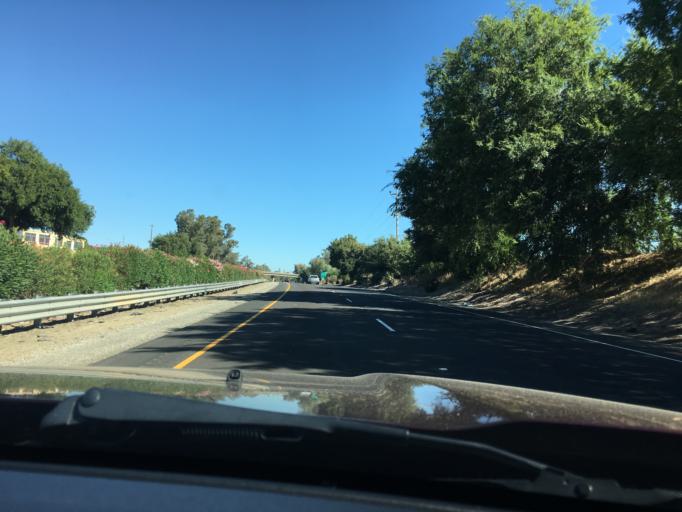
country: US
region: California
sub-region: San Joaquin County
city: Lodi
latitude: 38.1390
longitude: -121.2581
